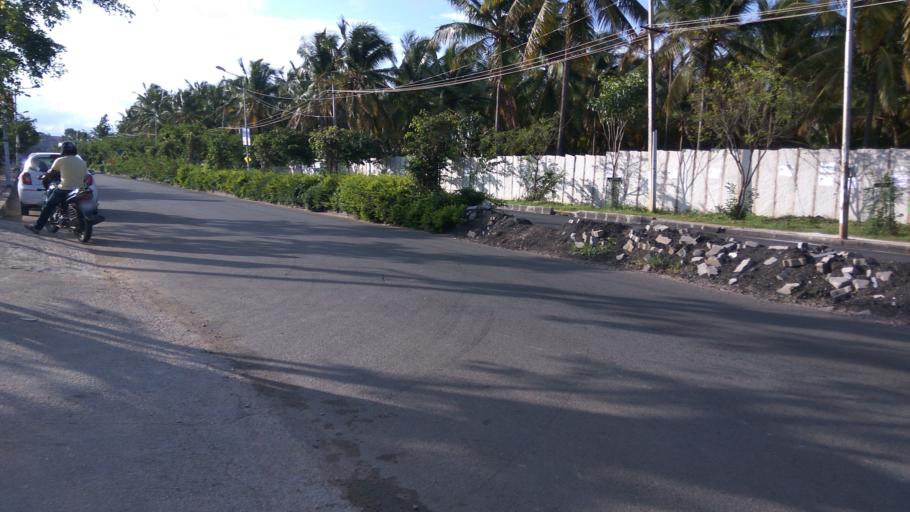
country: IN
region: Karnataka
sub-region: Bangalore Urban
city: Yelahanka
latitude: 13.1192
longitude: 77.6331
